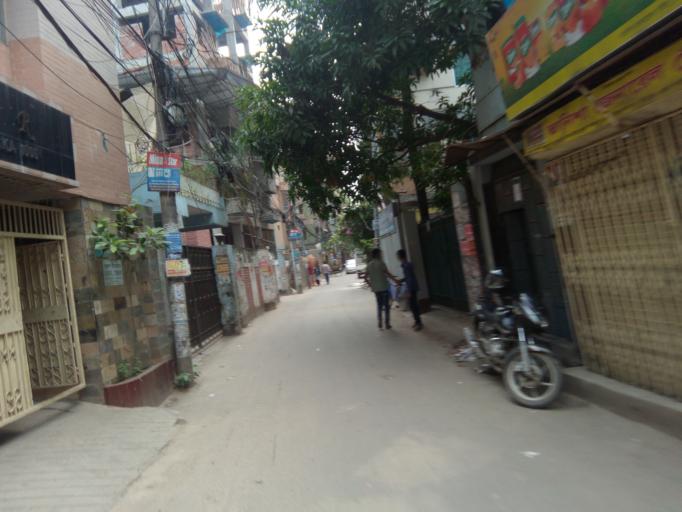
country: BD
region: Dhaka
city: Paltan
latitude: 23.7362
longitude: 90.4124
